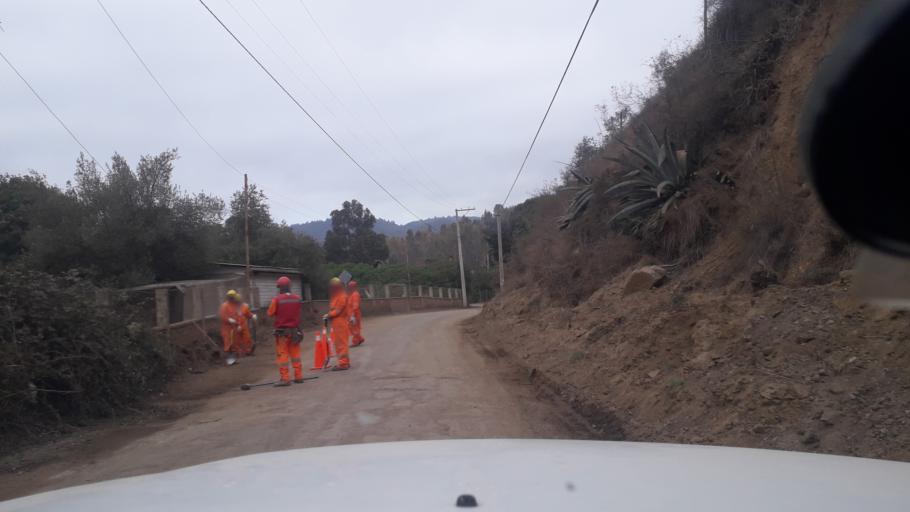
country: CL
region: Valparaiso
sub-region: Provincia de Valparaiso
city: Valparaiso
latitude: -33.1138
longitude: -71.6531
